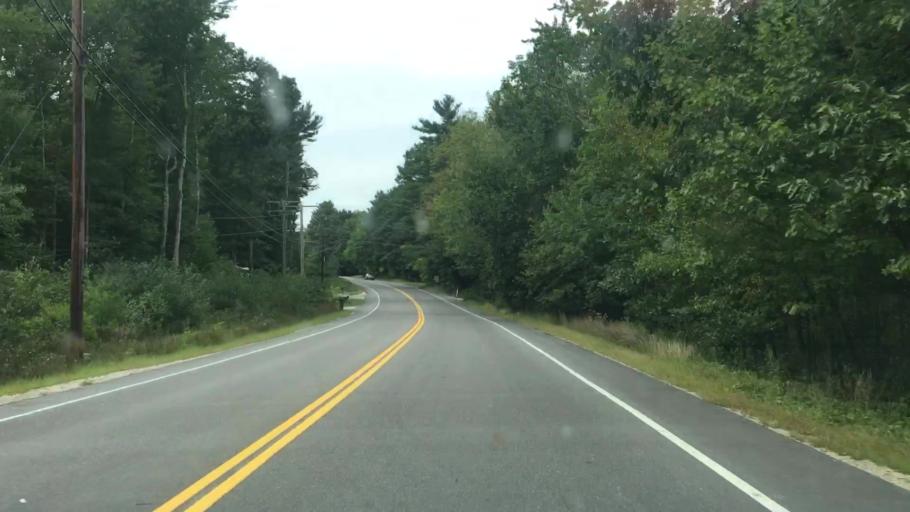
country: US
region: New Hampshire
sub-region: Strafford County
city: Madbury
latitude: 43.2050
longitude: -70.9701
